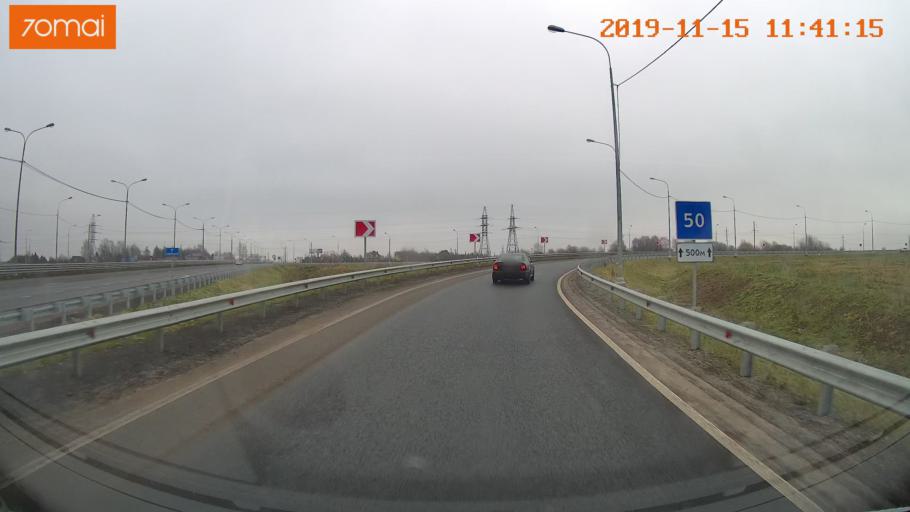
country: RU
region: Vologda
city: Vologda
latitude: 59.2128
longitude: 39.7702
